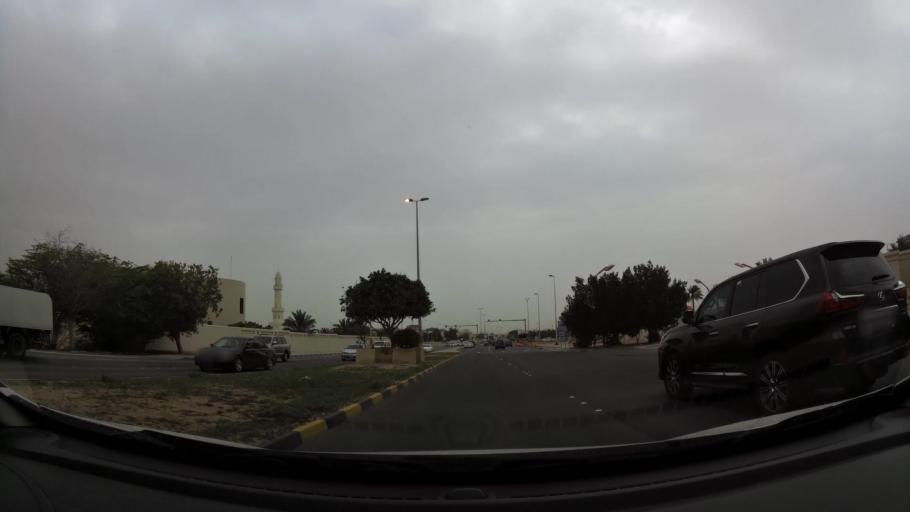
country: BH
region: Northern
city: Ar Rifa'
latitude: 26.1496
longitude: 50.5422
